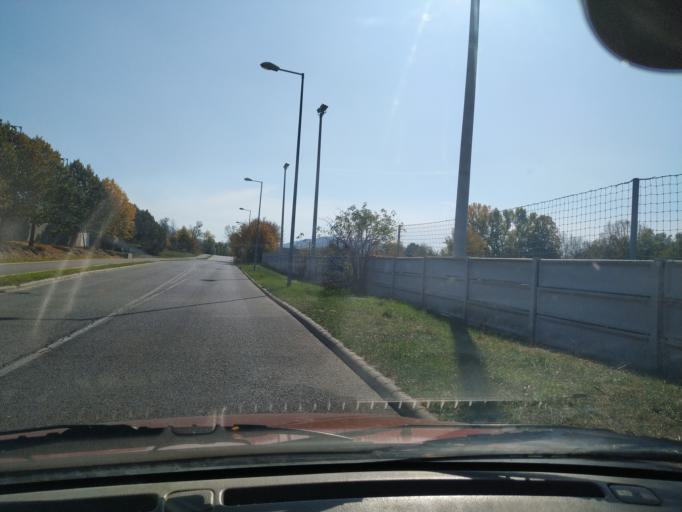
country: HU
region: Komarom-Esztergom
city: Esztergom
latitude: 47.7791
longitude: 18.7478
